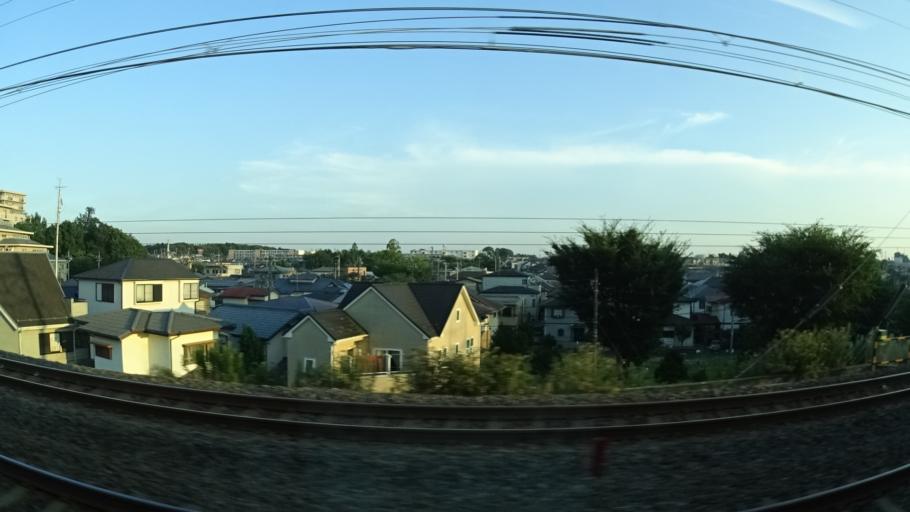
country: JP
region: Chiba
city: Abiko
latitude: 35.8729
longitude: 140.0329
